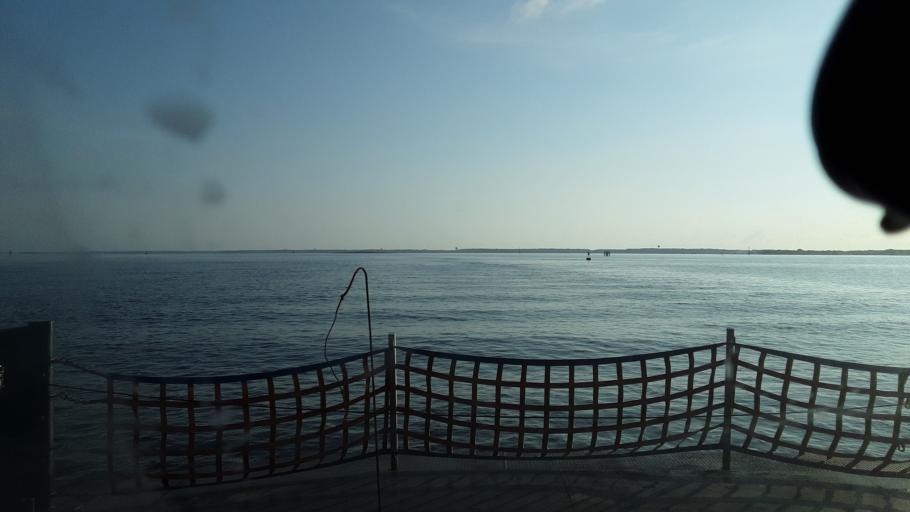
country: US
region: North Carolina
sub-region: New Hanover County
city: Kure Beach
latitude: 33.9577
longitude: -77.9562
